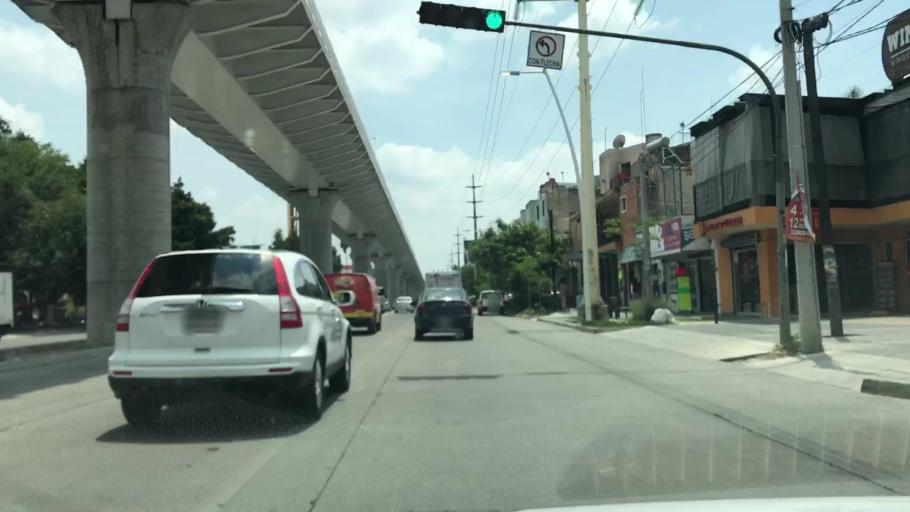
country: MX
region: Jalisco
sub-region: Zapopan
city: Zapopan
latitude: 20.7044
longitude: -103.3629
